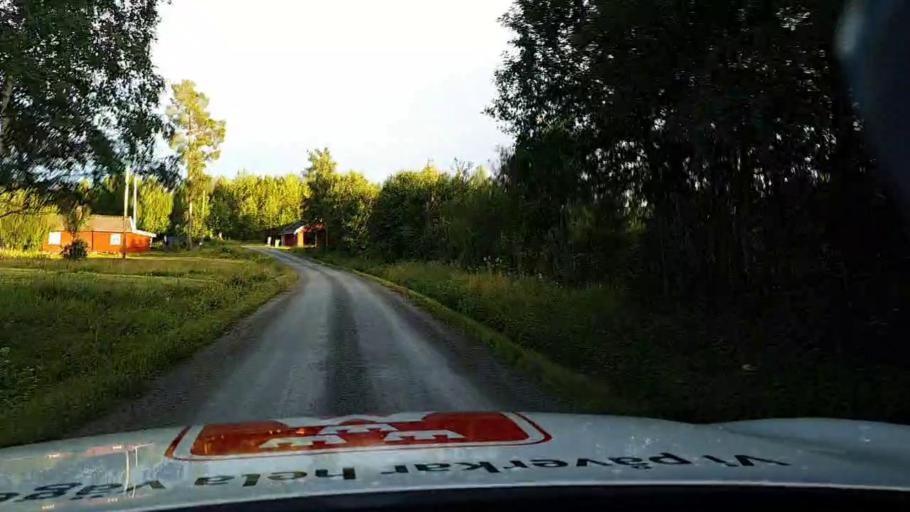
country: SE
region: Jaemtland
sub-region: Bergs Kommun
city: Hoverberg
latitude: 62.8536
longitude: 14.5370
